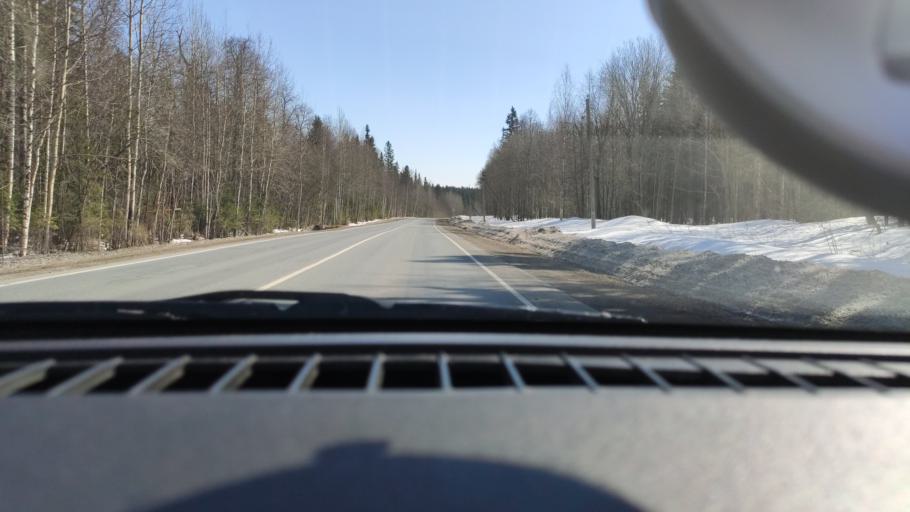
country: RU
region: Perm
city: Perm
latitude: 58.2083
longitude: 56.1930
